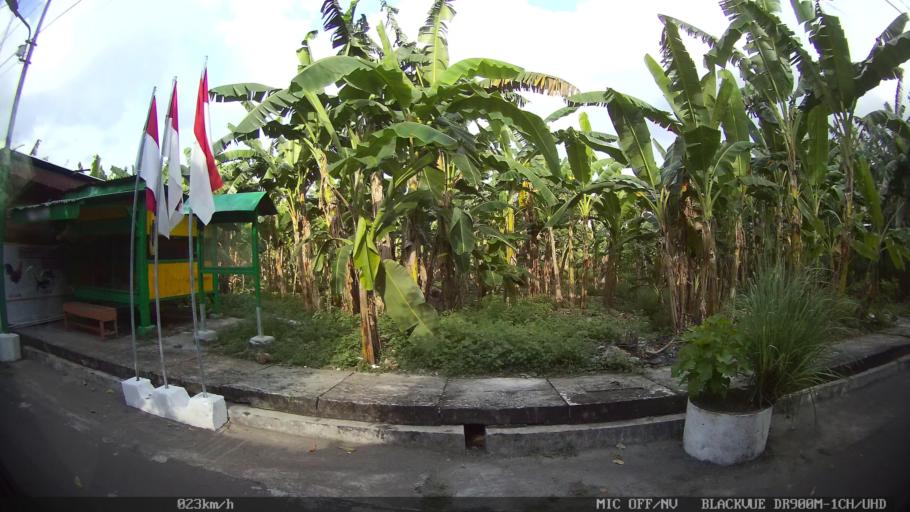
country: ID
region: Daerah Istimewa Yogyakarta
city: Kasihan
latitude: -7.8156
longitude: 110.3578
